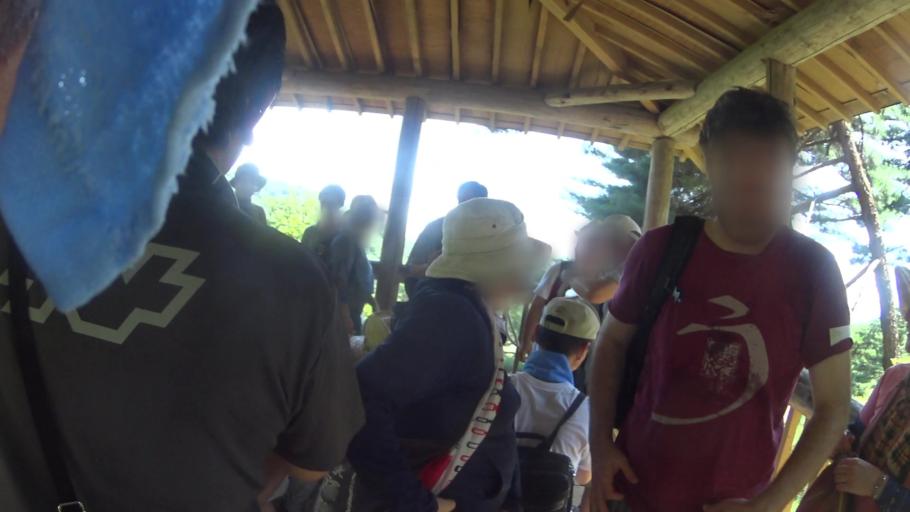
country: JP
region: Gunma
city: Ota
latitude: 36.3135
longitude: 139.3725
